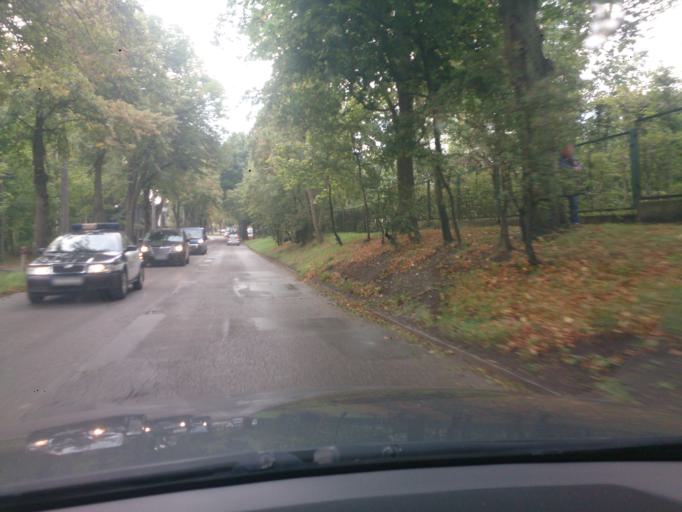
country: PL
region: Pomeranian Voivodeship
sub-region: Sopot
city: Sopot
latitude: 54.3966
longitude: 18.5649
